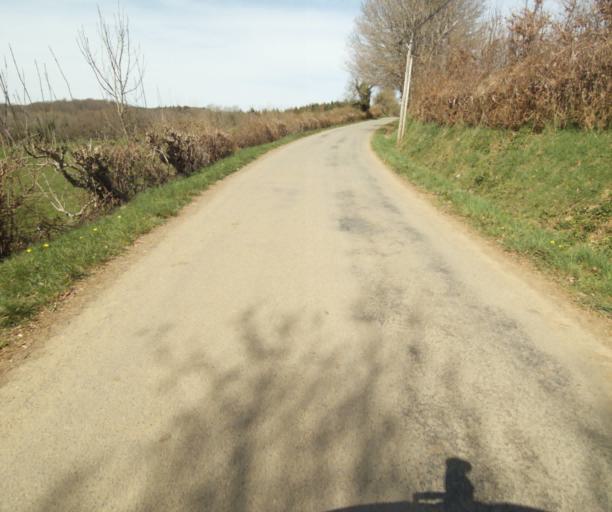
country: FR
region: Limousin
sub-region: Departement de la Correze
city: Seilhac
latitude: 45.3888
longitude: 1.7809
